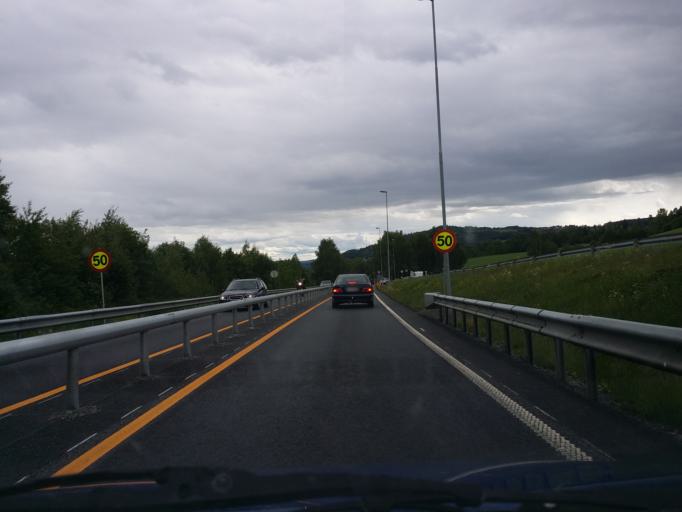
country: NO
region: Hedmark
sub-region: Ringsaker
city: Moelv
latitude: 60.9722
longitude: 10.5945
